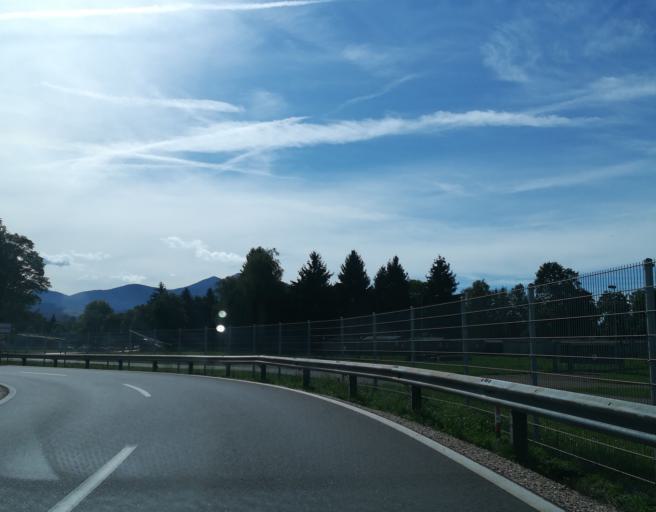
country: AT
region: Styria
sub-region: Politischer Bezirk Murtal
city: Flatschach
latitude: 47.2020
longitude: 14.7612
